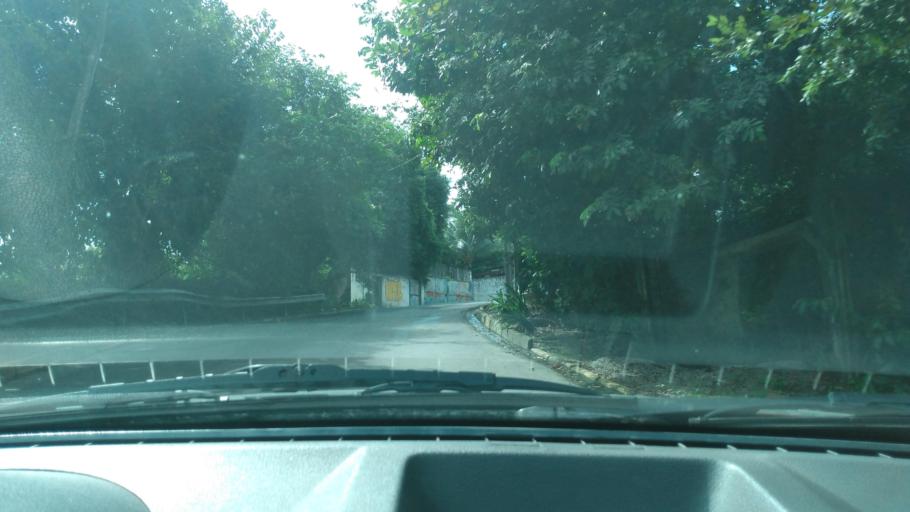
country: BR
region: Pernambuco
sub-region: Cabo De Santo Agostinho
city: Cabo
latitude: -8.3544
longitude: -34.9537
